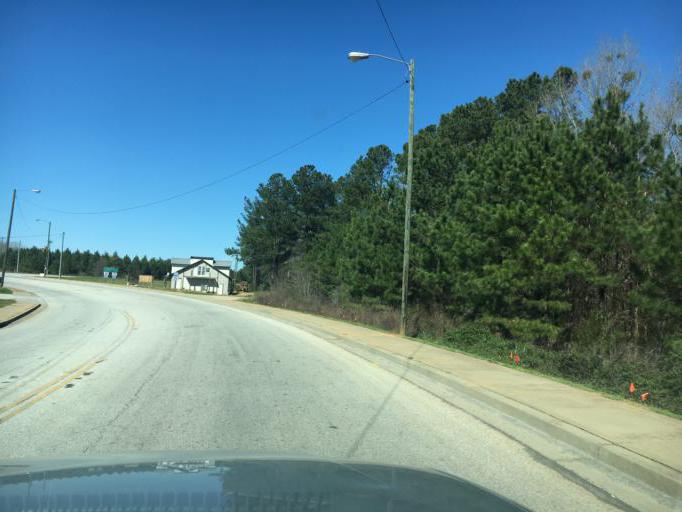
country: US
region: South Carolina
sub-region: Greenwood County
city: Ninety Six
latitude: 34.3157
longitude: -81.9908
